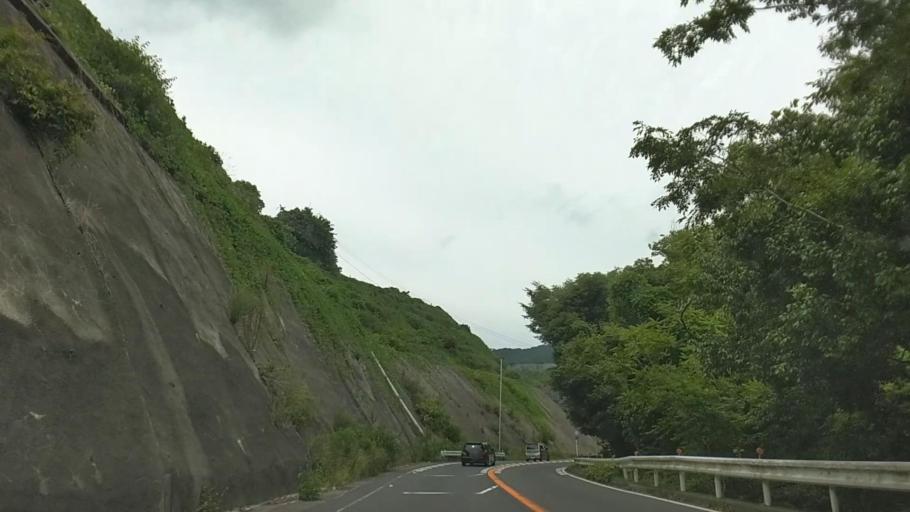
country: JP
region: Yamanashi
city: Uenohara
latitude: 35.6184
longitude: 139.1710
